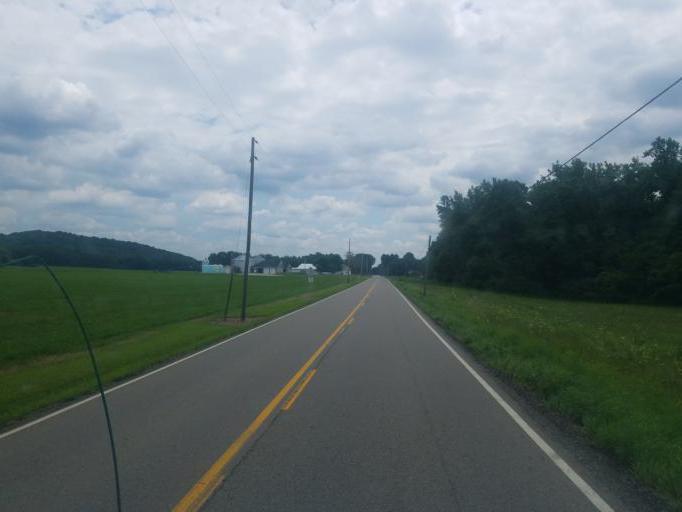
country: US
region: Ohio
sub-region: Licking County
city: Utica
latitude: 40.1515
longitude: -82.4515
